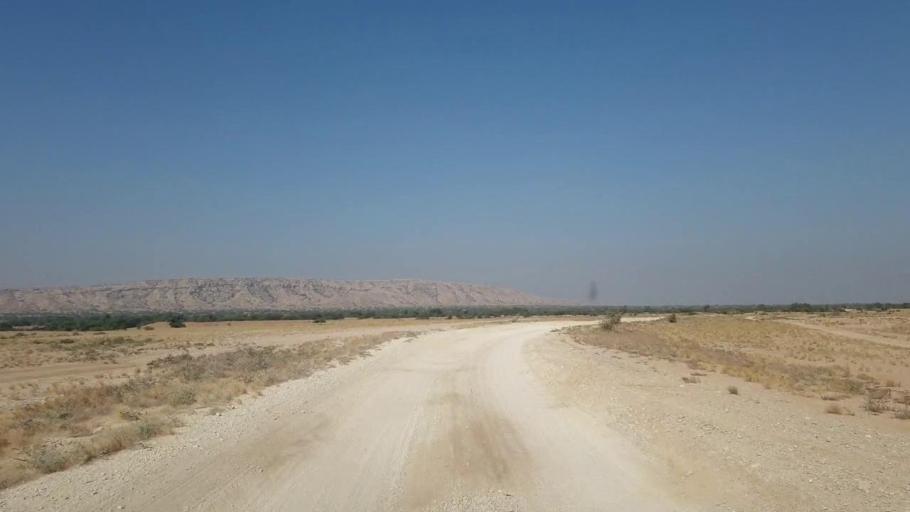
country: PK
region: Sindh
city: Jamshoro
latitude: 25.2632
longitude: 67.8048
